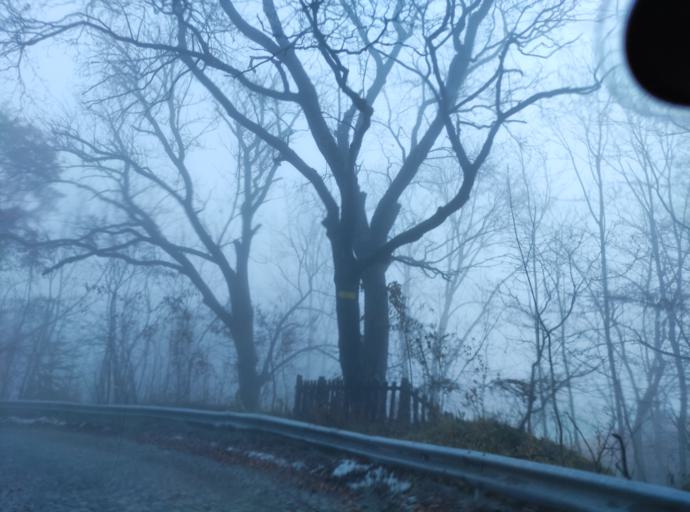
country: BG
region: Sofia-Capital
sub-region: Stolichna Obshtina
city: Sofia
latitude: 42.6191
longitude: 23.2980
